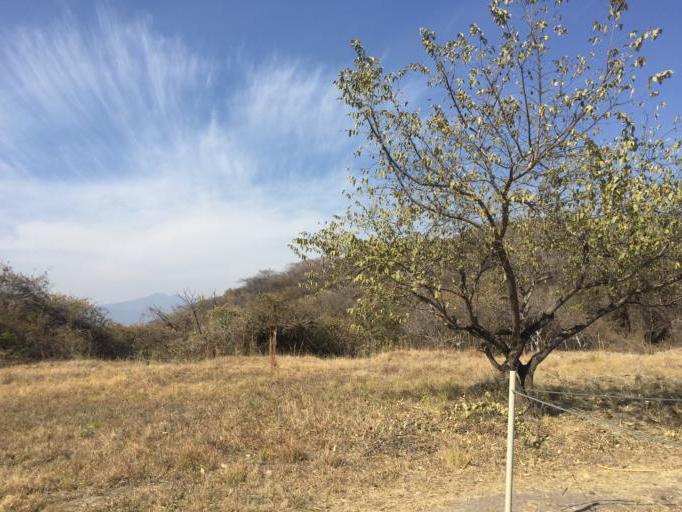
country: MX
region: Morelos
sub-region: Miacatlan
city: Xochicalco (Cirenio Longares)
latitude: 18.8018
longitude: -99.2991
